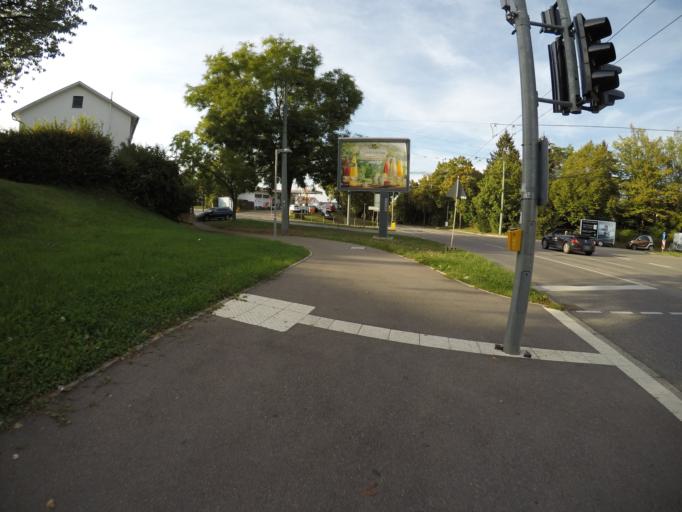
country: DE
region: Baden-Wuerttemberg
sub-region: Regierungsbezirk Stuttgart
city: Esslingen
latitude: 48.7244
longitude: 9.3019
